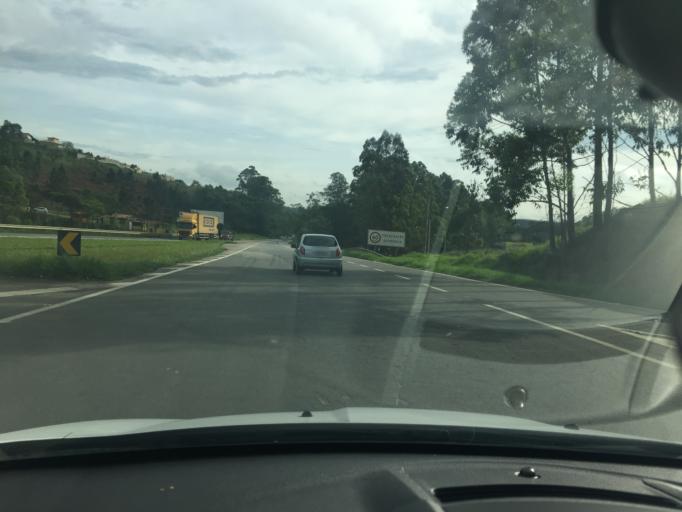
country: BR
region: Sao Paulo
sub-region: Campo Limpo Paulista
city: Campo Limpo Paulista
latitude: -23.1801
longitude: -46.7774
